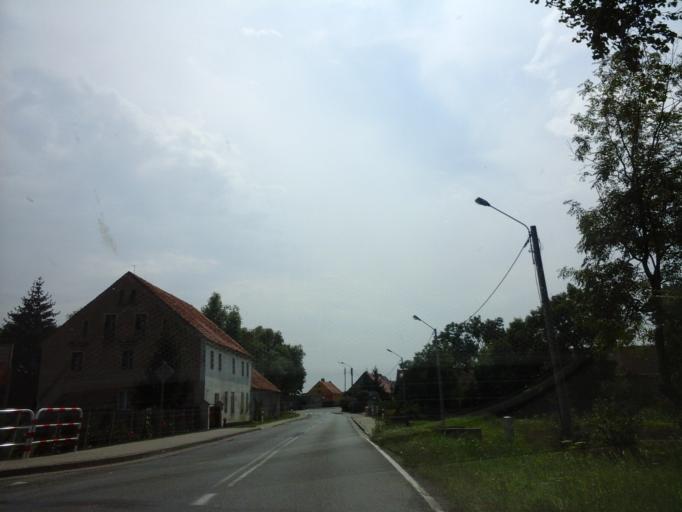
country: PL
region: Lower Silesian Voivodeship
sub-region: Powiat wroclawski
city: Zorawina
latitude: 50.8950
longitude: 17.0638
